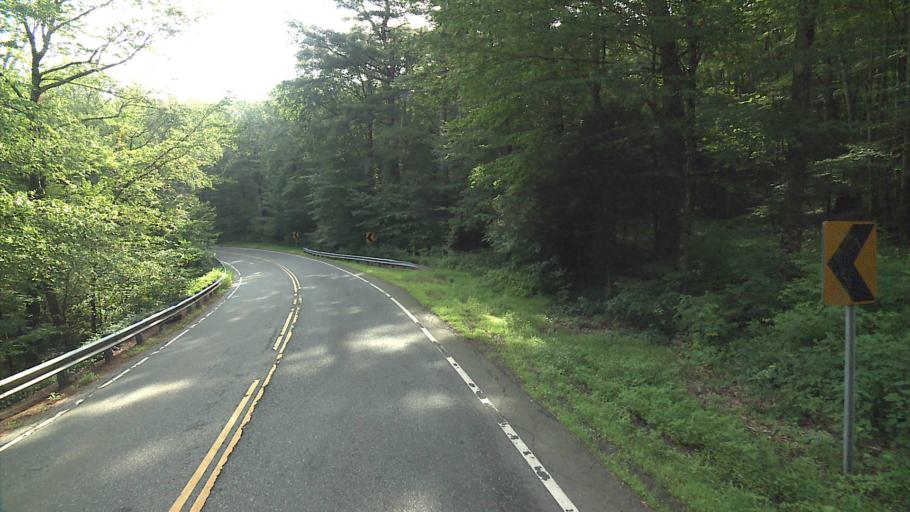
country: US
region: Connecticut
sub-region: Windham County
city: South Woodstock
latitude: 41.9815
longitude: -72.0244
